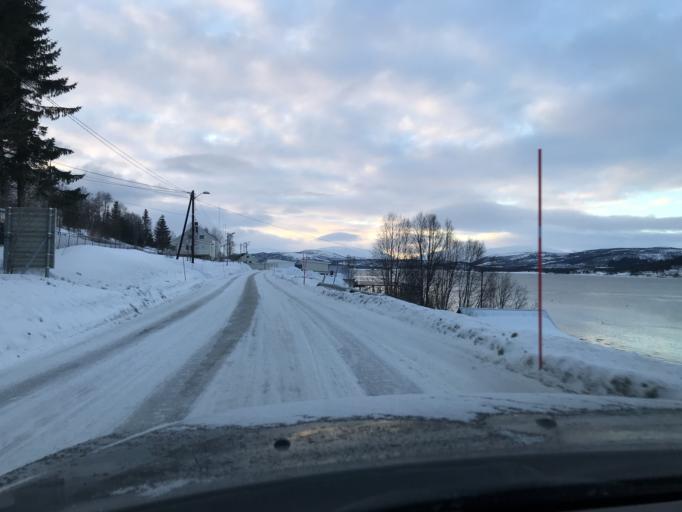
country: NO
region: Troms
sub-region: Lenvik
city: Finnsnes
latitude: 69.3423
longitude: 18.0962
